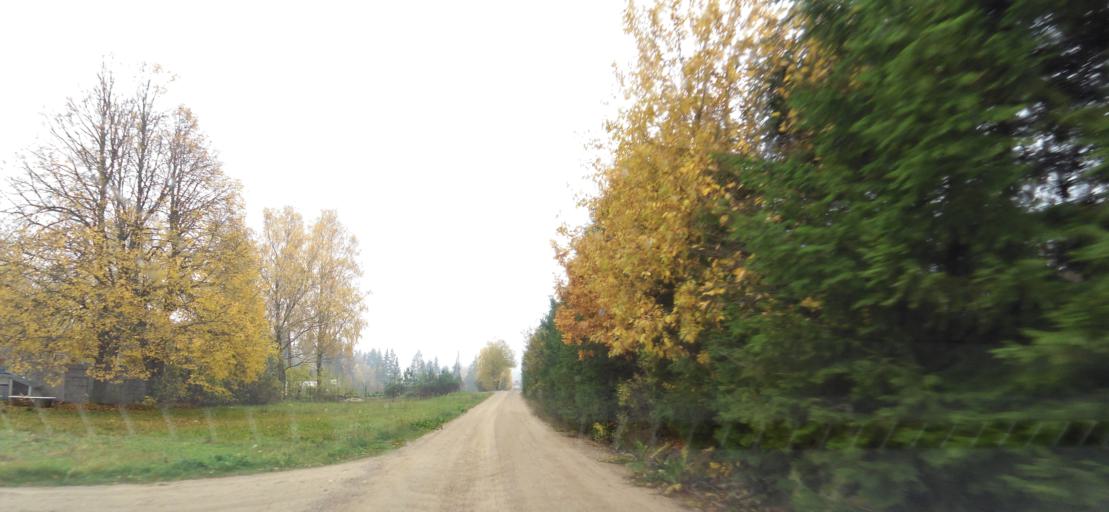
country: LT
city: Skaidiskes
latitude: 54.6200
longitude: 25.4712
